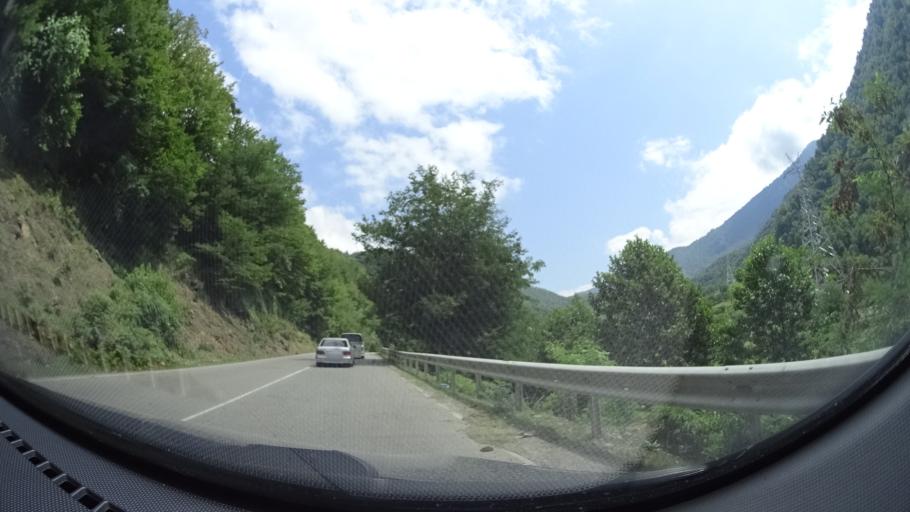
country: GE
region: Ajaria
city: Keda
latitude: 41.5685
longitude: 41.8441
